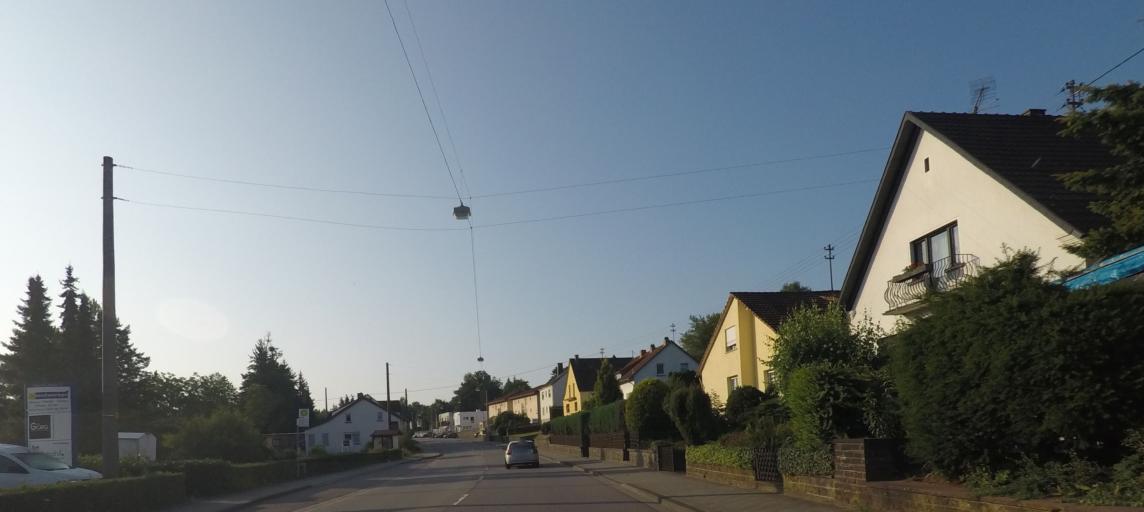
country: DE
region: Saarland
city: Lebach
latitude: 49.4044
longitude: 6.9140
